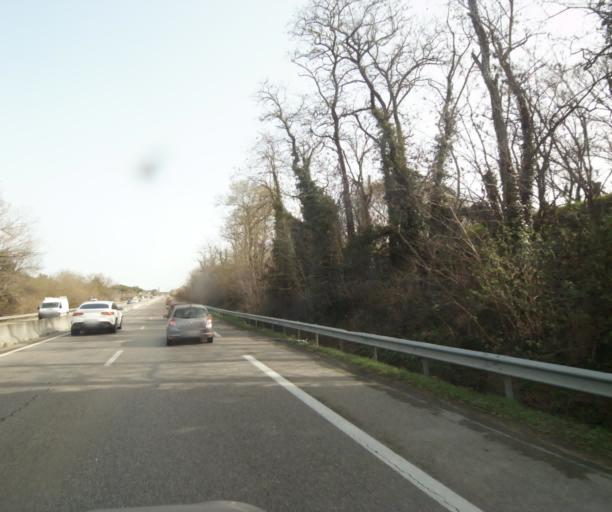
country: FR
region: Provence-Alpes-Cote d'Azur
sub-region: Departement des Bouches-du-Rhone
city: Simiane-Collongue
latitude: 43.4385
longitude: 5.4306
